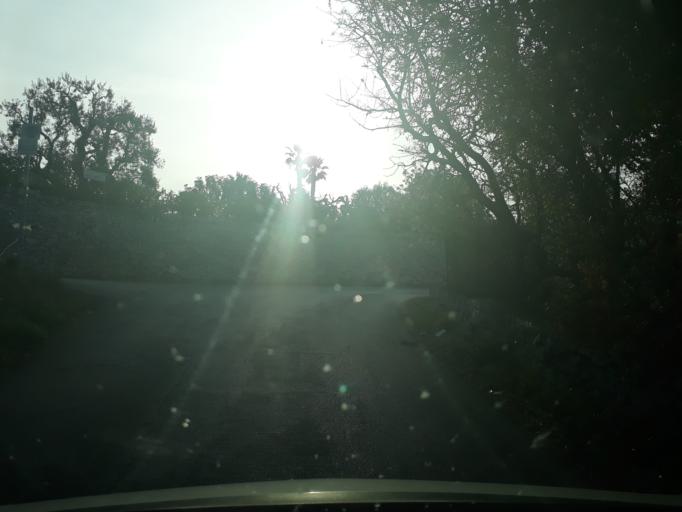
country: IT
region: Apulia
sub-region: Provincia di Brindisi
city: Lamie di Olimpie-Selva
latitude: 40.8297
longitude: 17.3341
